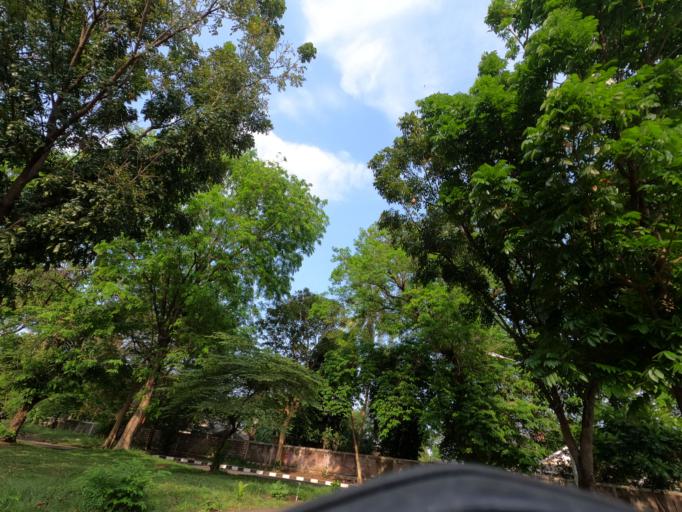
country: ID
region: West Java
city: Lembang
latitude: -6.5754
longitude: 107.7635
